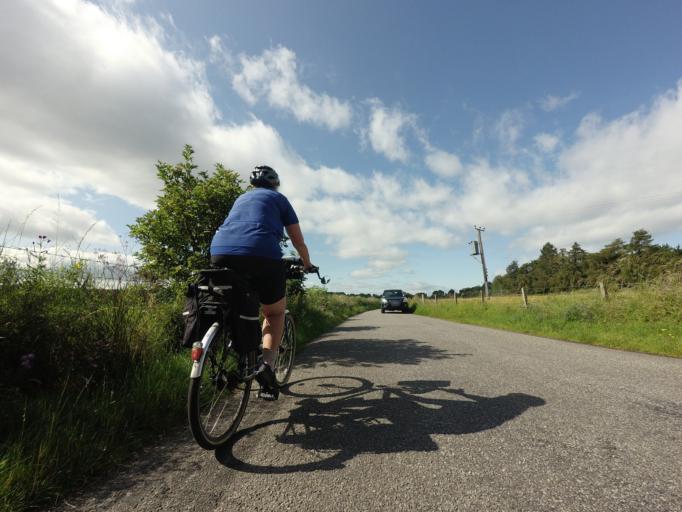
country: GB
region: Scotland
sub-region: Highland
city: Nairn
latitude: 57.5733
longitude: -3.8639
